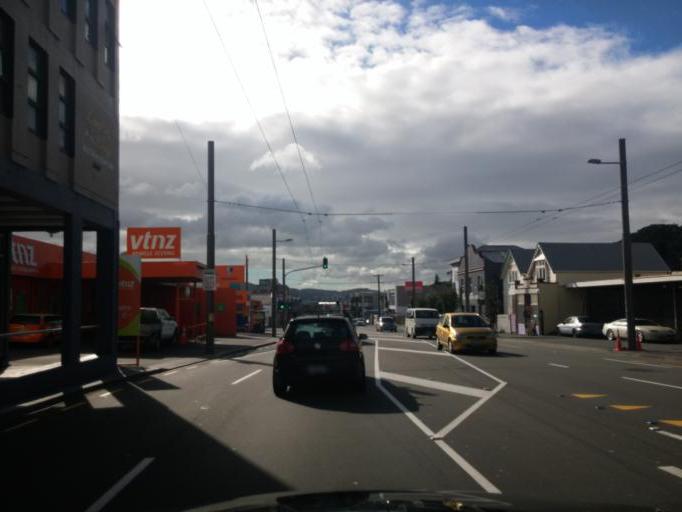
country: NZ
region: Wellington
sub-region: Wellington City
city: Wellington
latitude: -41.3070
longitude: 174.7779
